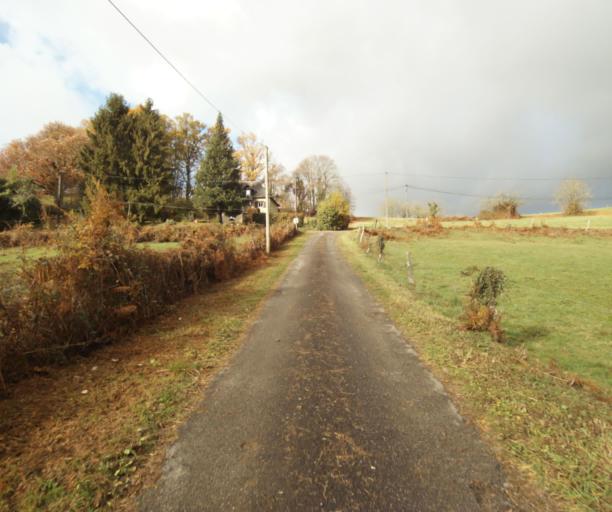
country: FR
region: Limousin
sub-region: Departement de la Correze
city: Sainte-Fereole
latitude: 45.2196
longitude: 1.6256
